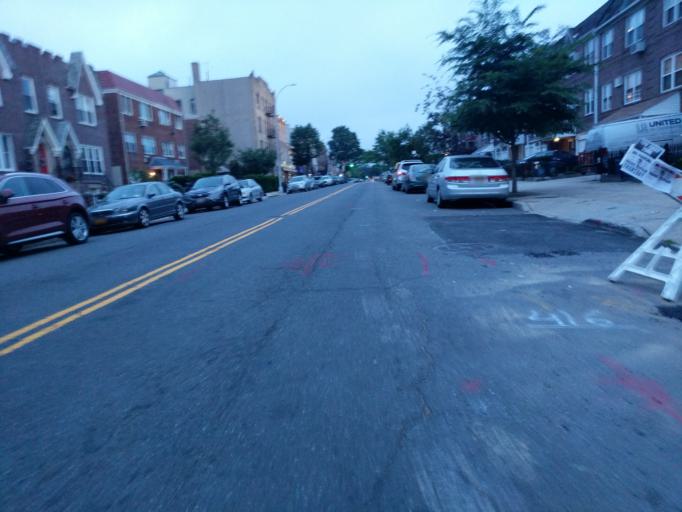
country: US
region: New York
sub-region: Queens County
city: Long Island City
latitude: 40.7739
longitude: -73.9049
